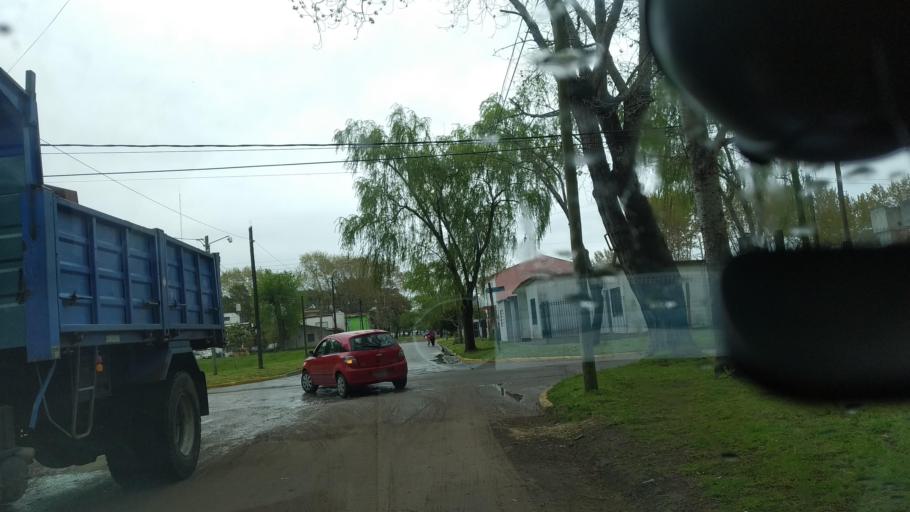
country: AR
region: Buenos Aires
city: Mar del Tuyu
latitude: -36.5324
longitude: -56.7128
